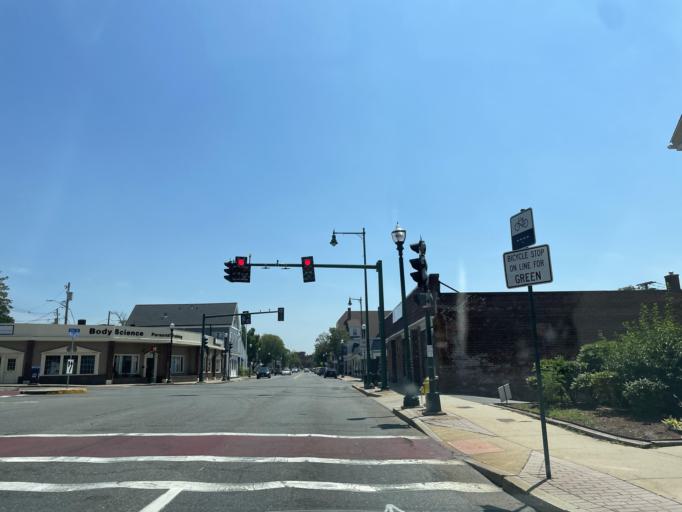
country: US
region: Massachusetts
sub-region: Norfolk County
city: Braintree
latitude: 42.2213
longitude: -71.0042
